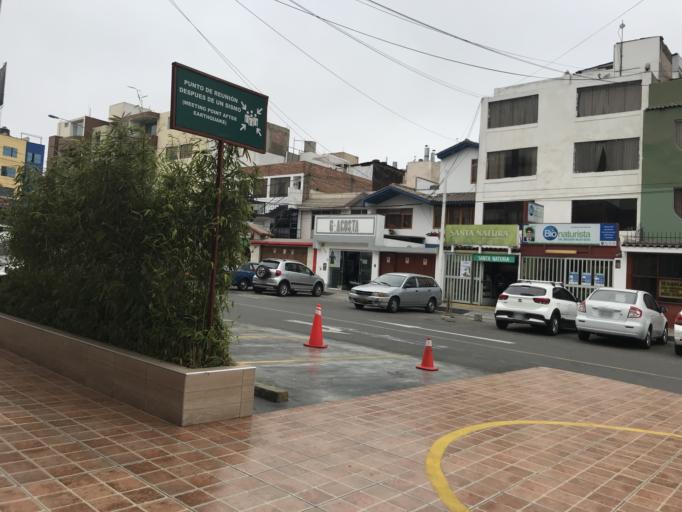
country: PE
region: Callao
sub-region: Callao
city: Callao
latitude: -12.0754
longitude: -77.0831
